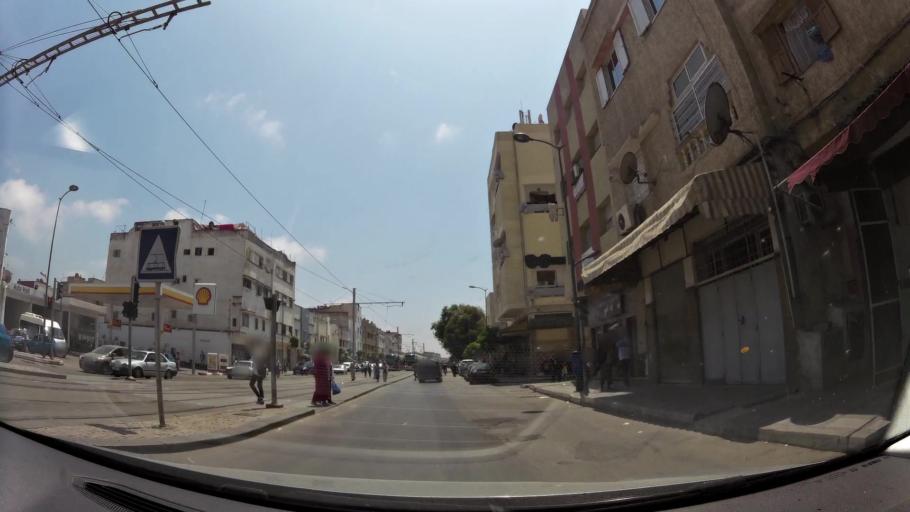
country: MA
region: Rabat-Sale-Zemmour-Zaer
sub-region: Rabat
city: Rabat
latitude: 34.0104
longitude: -6.8597
